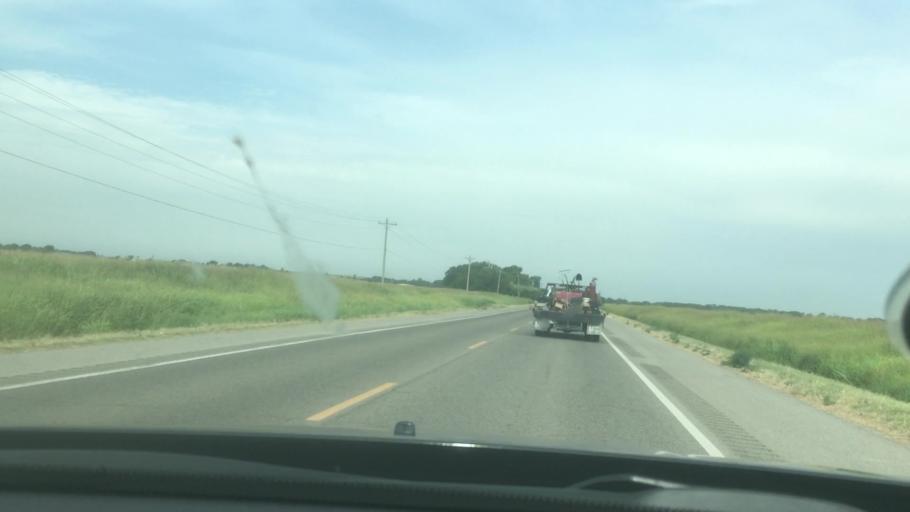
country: US
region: Oklahoma
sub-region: Garvin County
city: Lindsay
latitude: 34.8247
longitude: -97.5396
